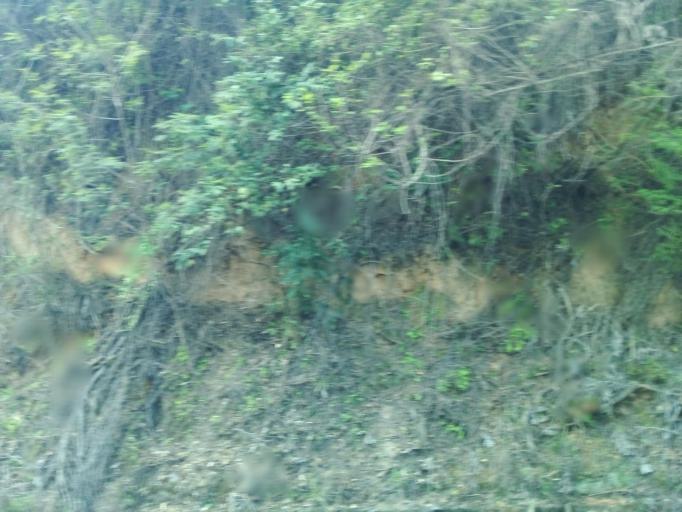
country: BR
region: Minas Gerais
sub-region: Governador Valadares
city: Governador Valadares
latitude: -18.9139
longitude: -42.0016
